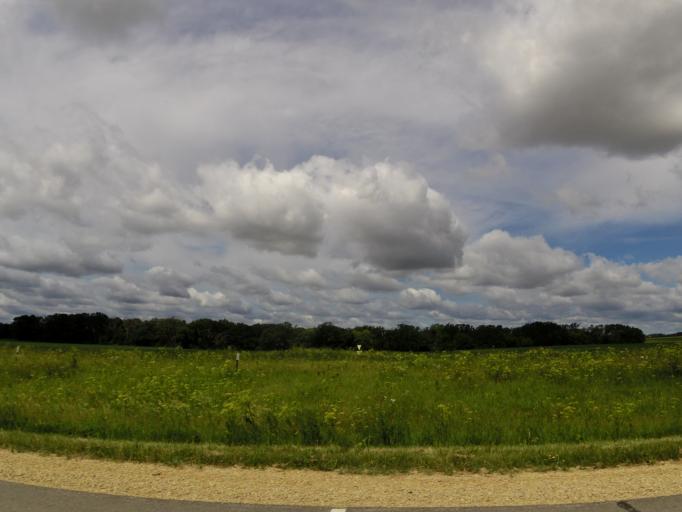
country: US
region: Minnesota
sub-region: Olmsted County
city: Stewartville
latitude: 43.7526
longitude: -92.4792
